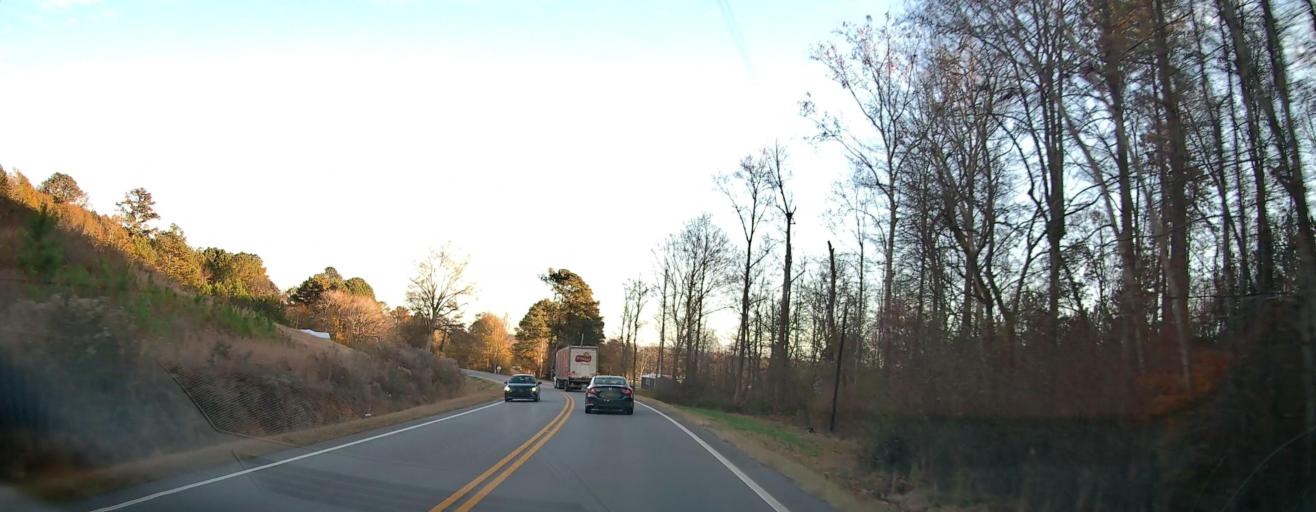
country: US
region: Alabama
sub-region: Saint Clair County
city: Steele
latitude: 34.0695
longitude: -86.3122
